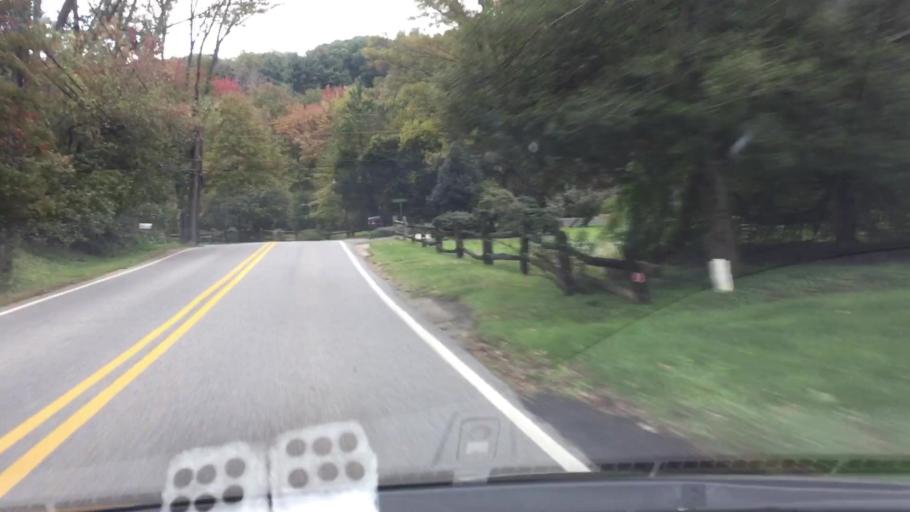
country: US
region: Pennsylvania
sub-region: Delaware County
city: Lima
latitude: 39.9285
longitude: -75.4260
